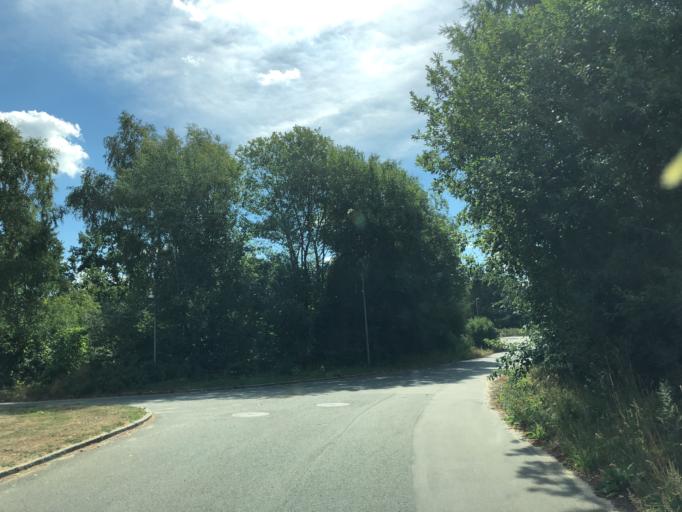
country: DK
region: Central Jutland
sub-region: Silkeborg Kommune
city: Silkeborg
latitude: 56.1600
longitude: 9.5008
